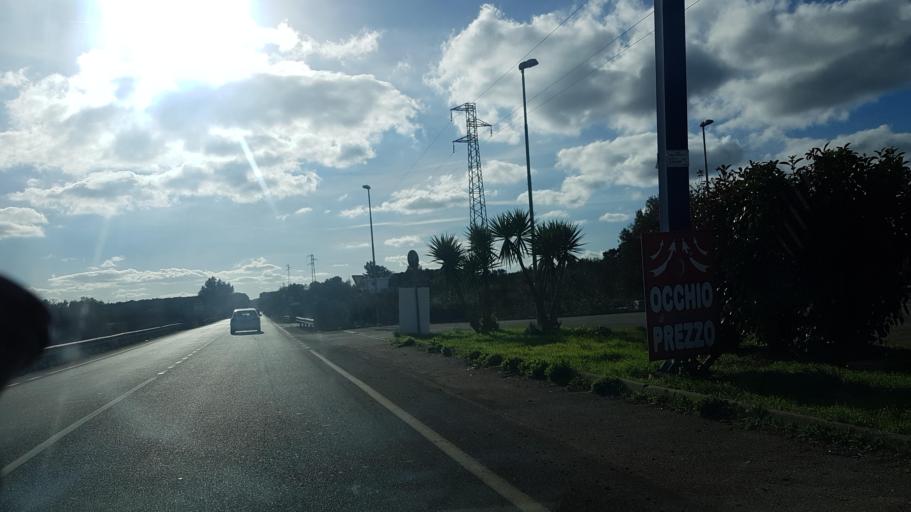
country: IT
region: Apulia
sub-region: Provincia di Brindisi
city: Ceglie Messapica
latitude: 40.6832
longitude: 17.5479
